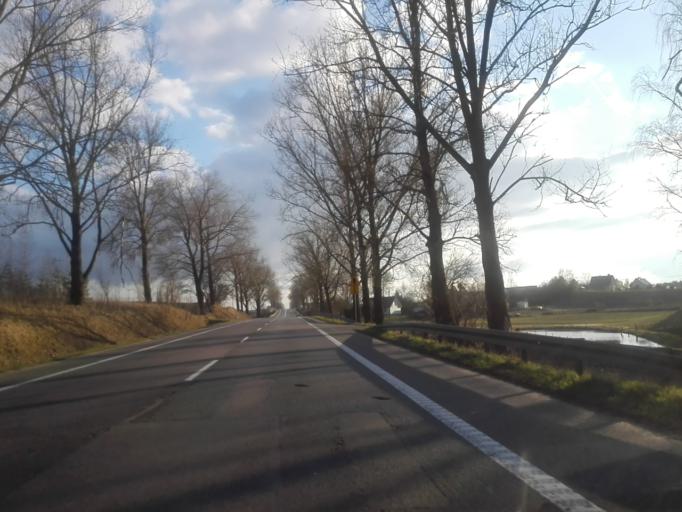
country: PL
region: Podlasie
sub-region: Suwalki
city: Suwalki
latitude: 54.1403
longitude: 22.9601
